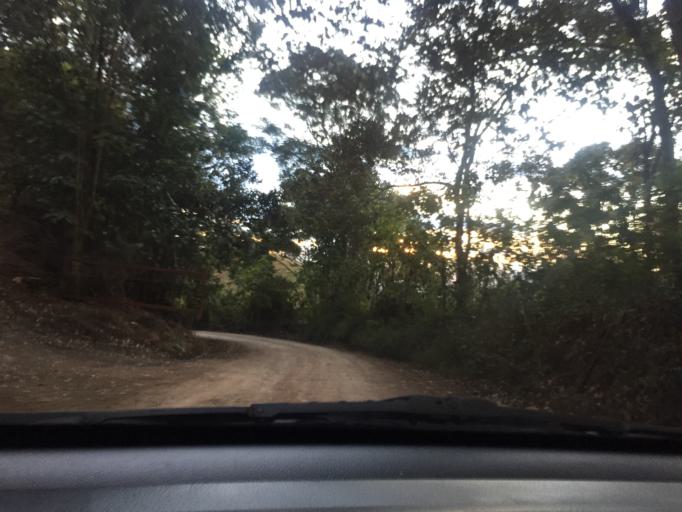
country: CO
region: Cundinamarca
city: Zipacon
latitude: 4.7049
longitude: -74.4070
